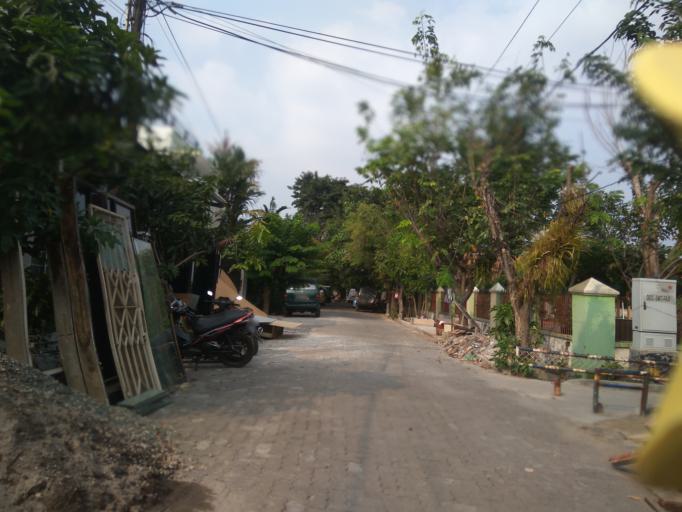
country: ID
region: Central Java
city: Semarang
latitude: -6.9751
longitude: 110.3924
